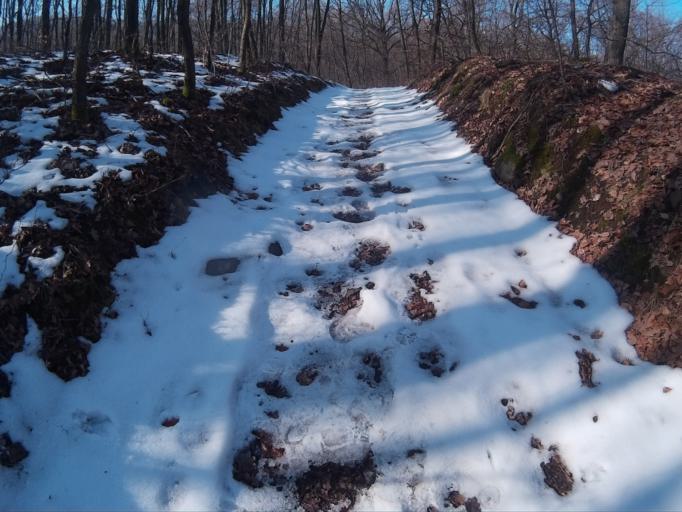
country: HU
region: Nograd
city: Paszto
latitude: 47.9960
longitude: 19.6798
